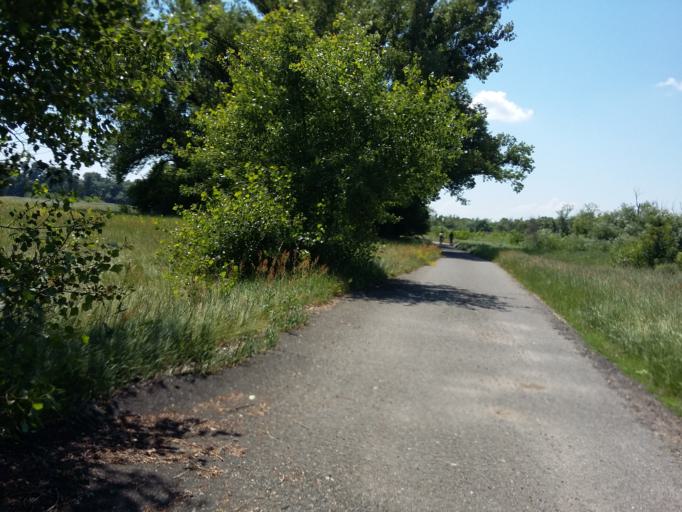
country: AT
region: Lower Austria
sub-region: Politischer Bezirk Ganserndorf
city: Marchegg
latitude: 48.2473
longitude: 16.9510
